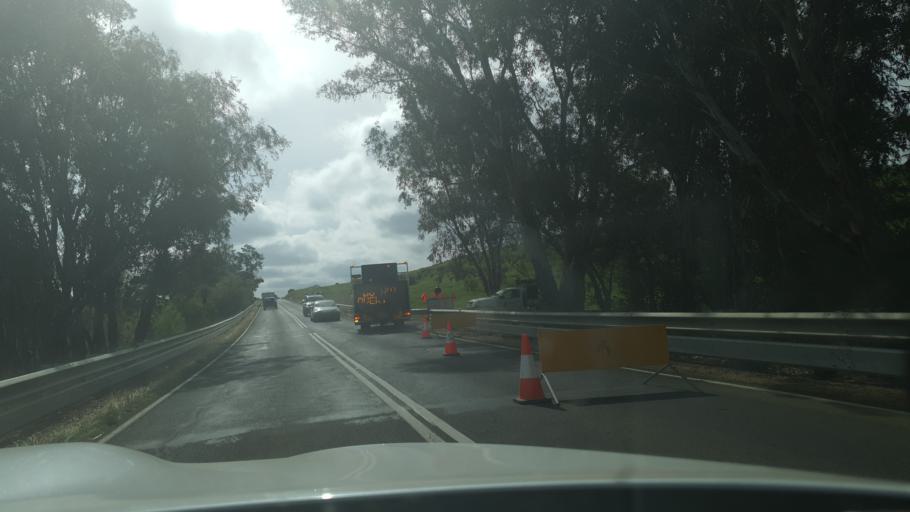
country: AU
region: Victoria
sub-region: Central Goldfields
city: Maryborough
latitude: -37.2134
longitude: 143.7267
